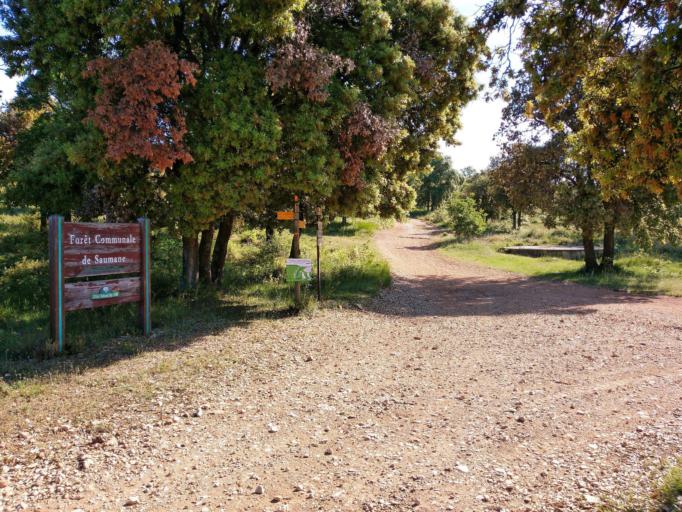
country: FR
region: Provence-Alpes-Cote d'Azur
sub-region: Departement du Vaucluse
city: Venasque
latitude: 43.9422
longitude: 5.1577
